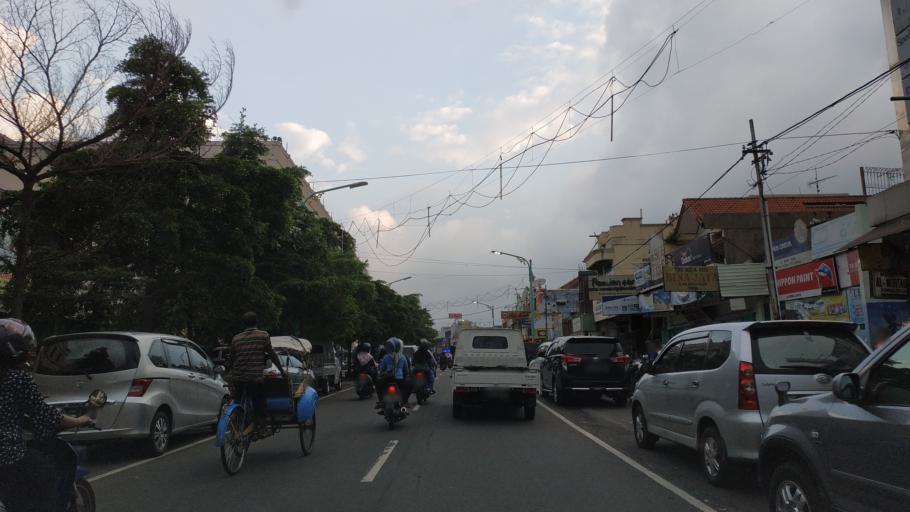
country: ID
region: Central Java
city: Salatiga
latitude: -7.3274
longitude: 110.5046
